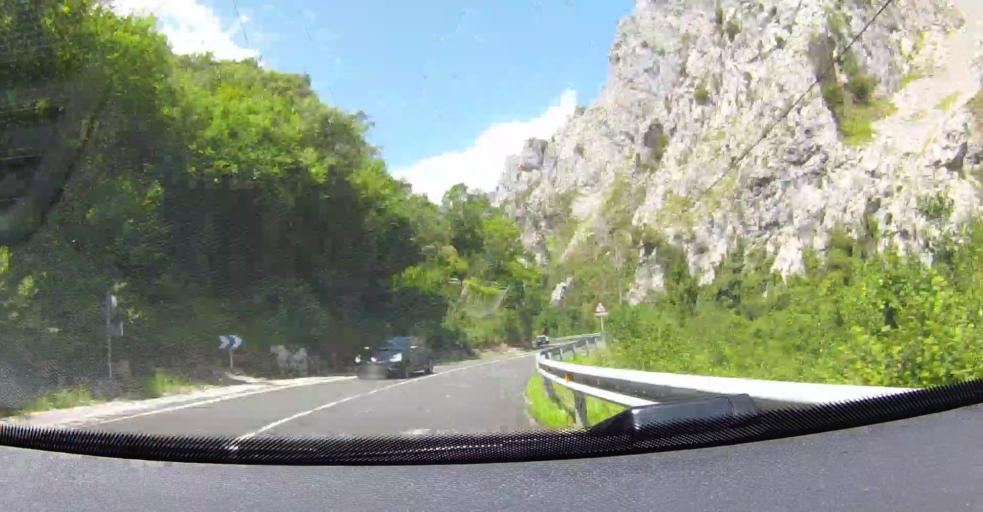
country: ES
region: Cantabria
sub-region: Provincia de Cantabria
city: Tresviso
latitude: 43.2637
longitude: -4.6228
